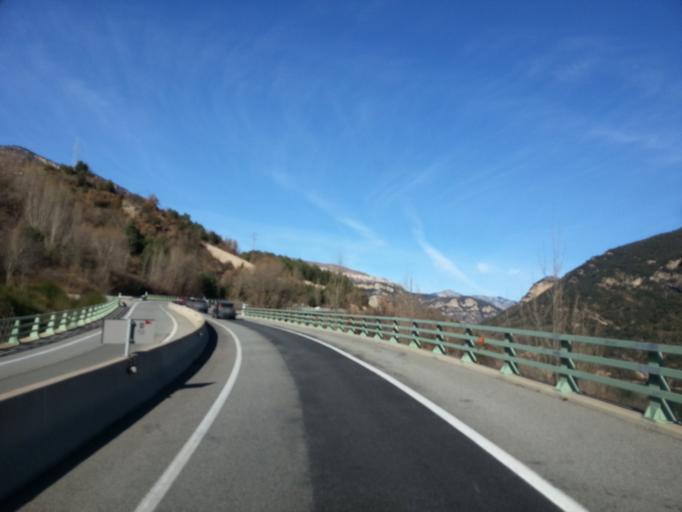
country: ES
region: Catalonia
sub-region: Provincia de Barcelona
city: Berga
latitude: 42.1482
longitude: 1.8665
